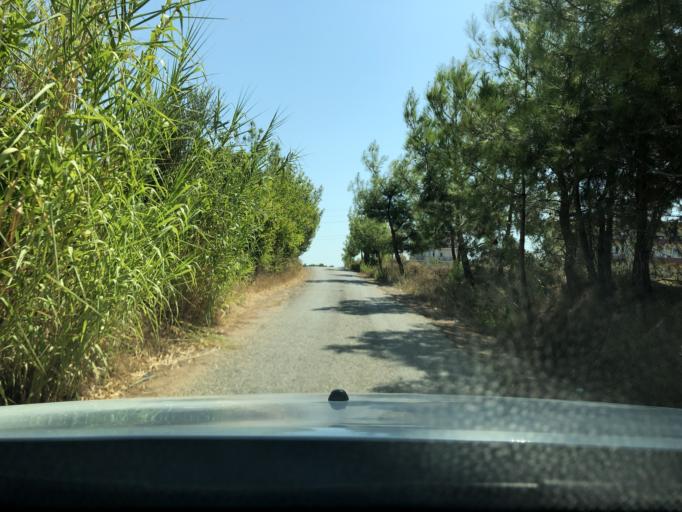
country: TR
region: Antalya
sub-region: Manavgat
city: Manavgat
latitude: 36.8041
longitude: 31.4747
